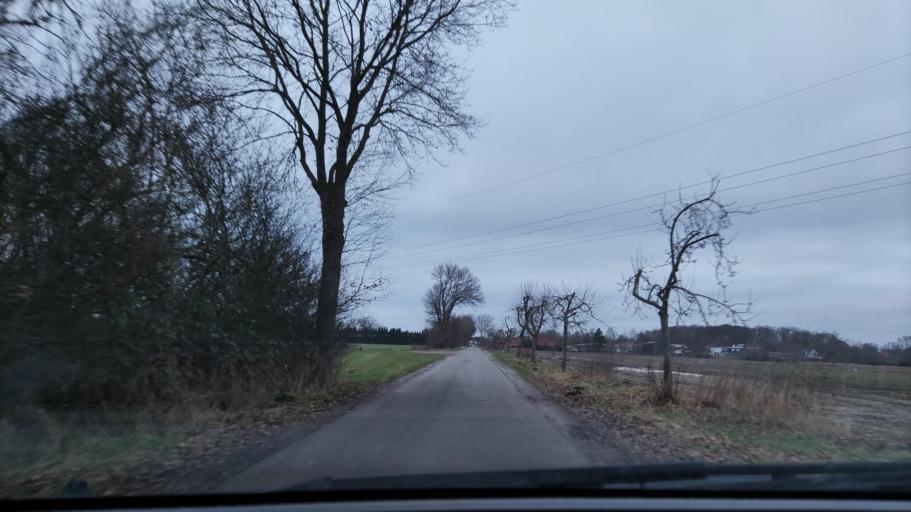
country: DE
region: Lower Saxony
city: Reppenstedt
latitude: 53.2398
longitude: 10.3501
